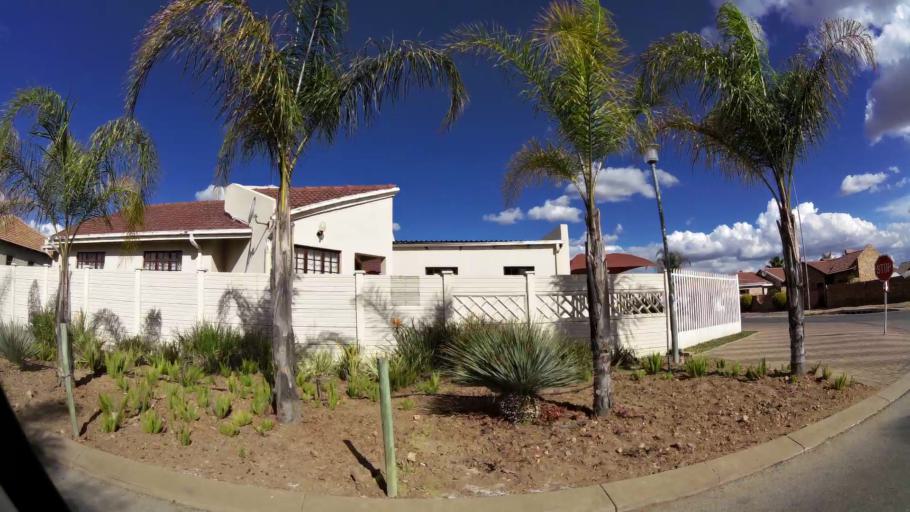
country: ZA
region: Limpopo
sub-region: Capricorn District Municipality
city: Polokwane
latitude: -23.8832
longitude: 29.4742
